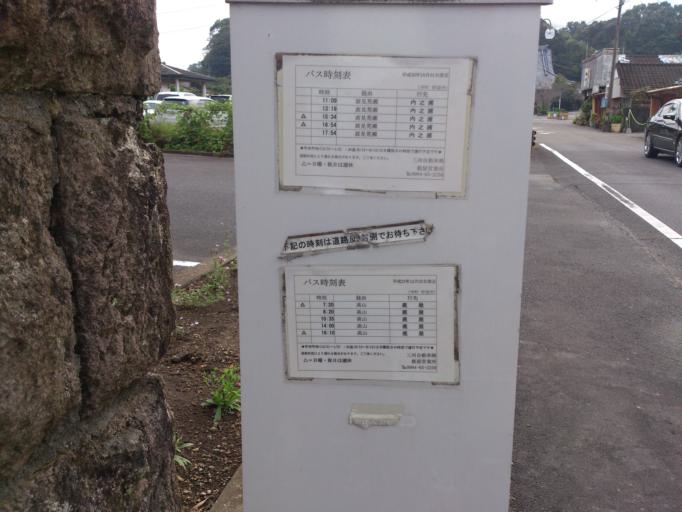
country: JP
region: Kagoshima
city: Kanoya
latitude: 31.3472
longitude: 130.9518
